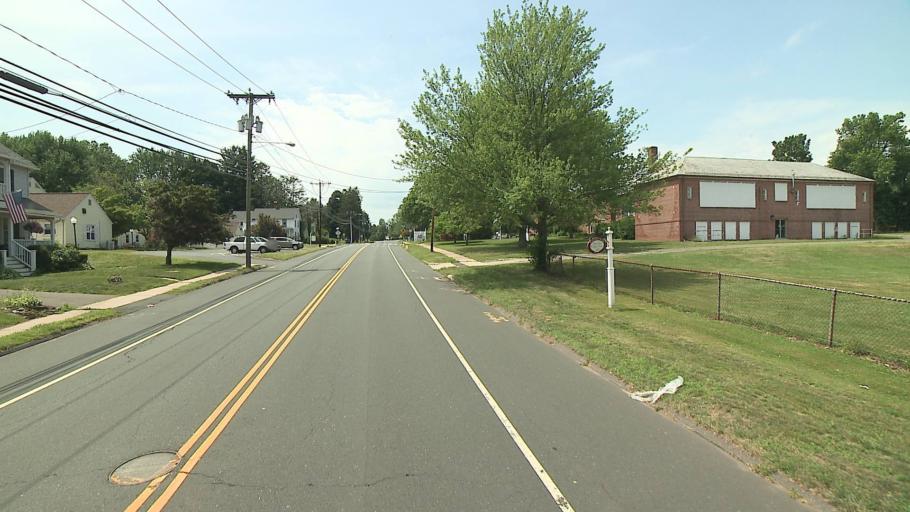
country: US
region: Connecticut
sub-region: Hartford County
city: Suffield Depot
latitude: 41.9806
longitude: -72.6476
